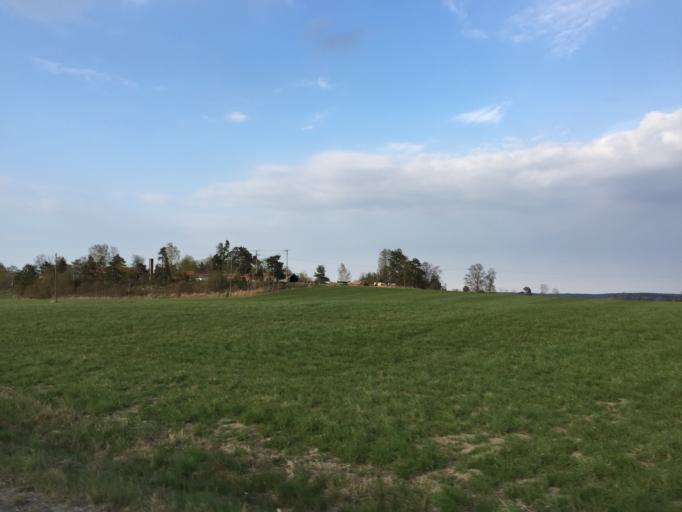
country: SE
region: Stockholm
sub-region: Sodertalje Kommun
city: Pershagen
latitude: 59.0788
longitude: 17.6083
